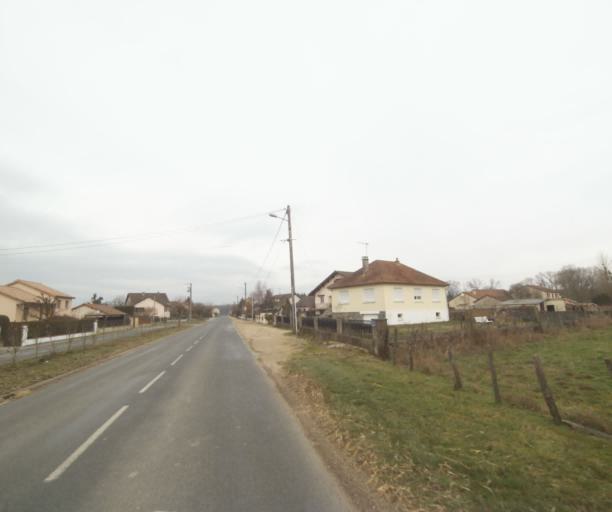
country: FR
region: Champagne-Ardenne
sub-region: Departement de la Haute-Marne
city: Villiers-en-Lieu
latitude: 48.6791
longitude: 4.8858
